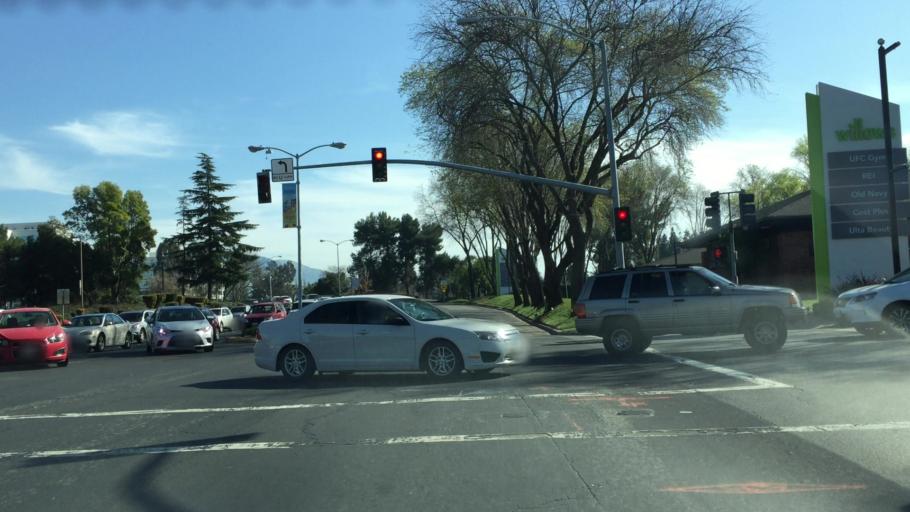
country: US
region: California
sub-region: Contra Costa County
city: Pleasant Hill
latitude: 37.9708
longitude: -122.0554
